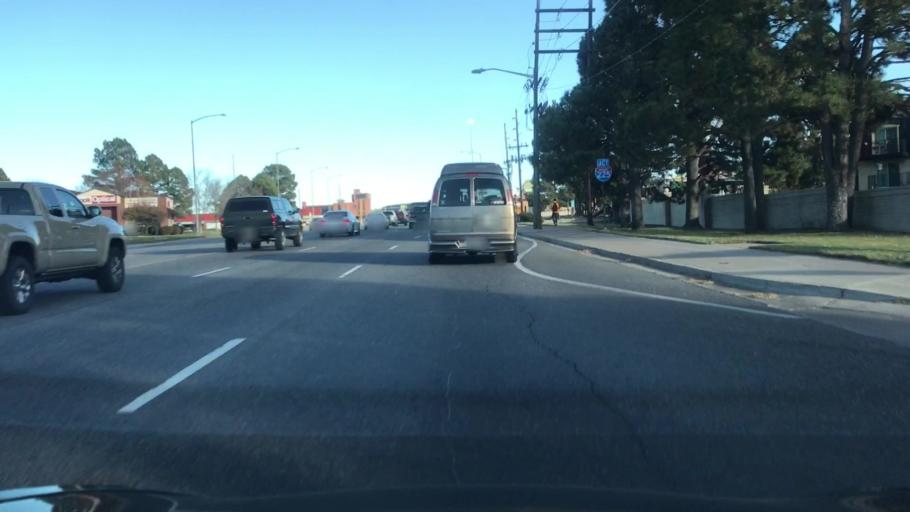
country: US
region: Colorado
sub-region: Adams County
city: Aurora
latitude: 39.6596
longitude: -104.8515
